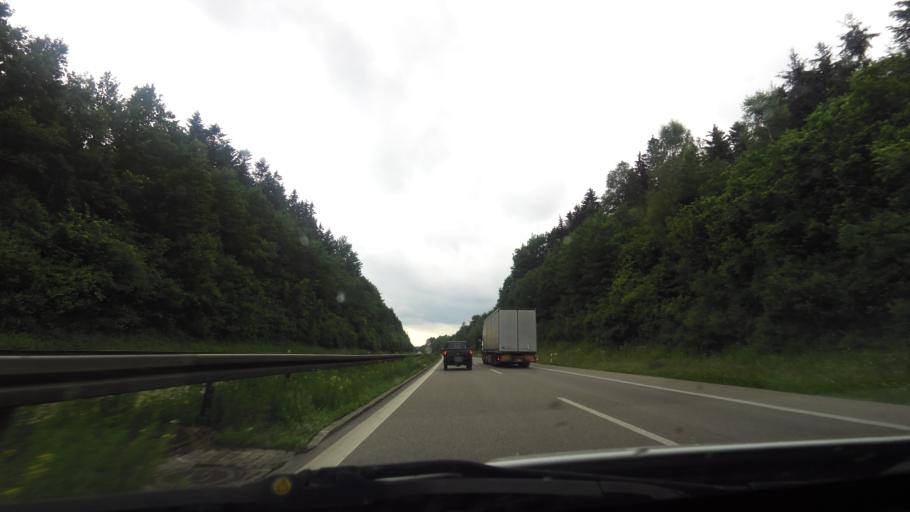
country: DE
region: Bavaria
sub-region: Swabia
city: Buxheim
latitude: 47.9866
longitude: 10.1317
